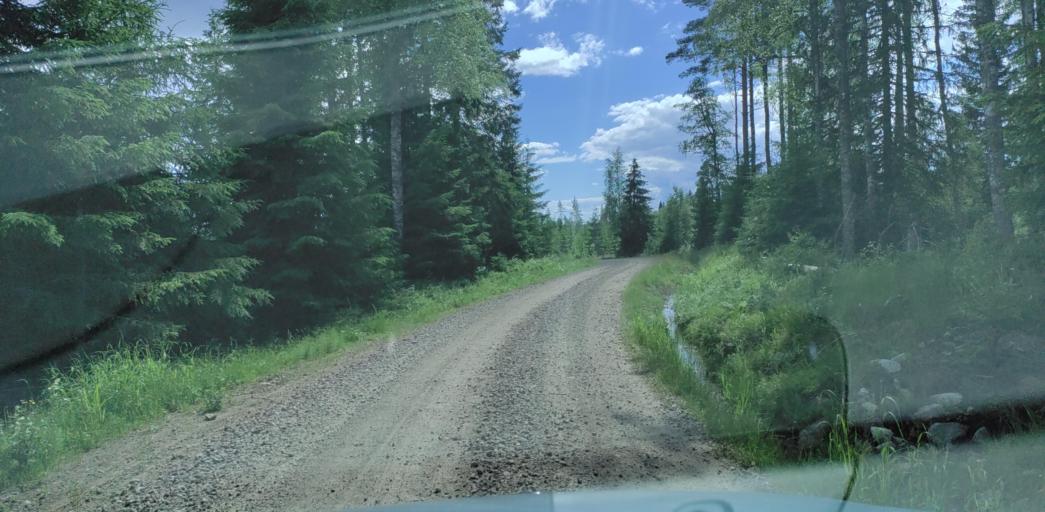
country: SE
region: Vaermland
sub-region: Hagfors Kommun
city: Ekshaerad
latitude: 60.0483
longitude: 13.3095
